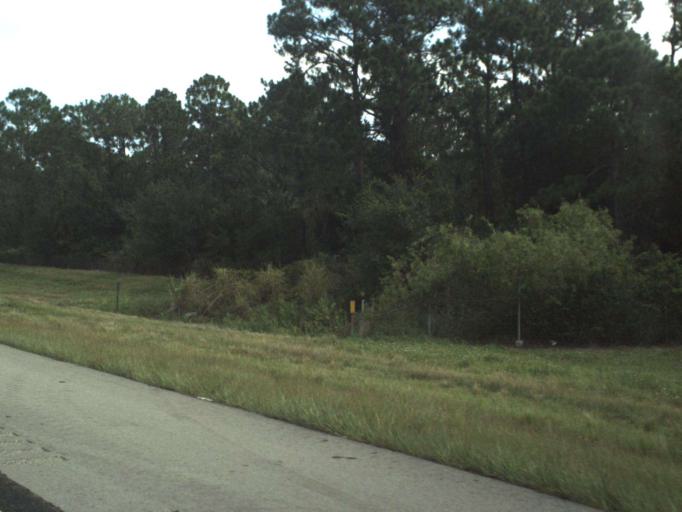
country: US
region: Florida
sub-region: Saint Lucie County
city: Lakewood Park
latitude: 27.4845
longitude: -80.4348
